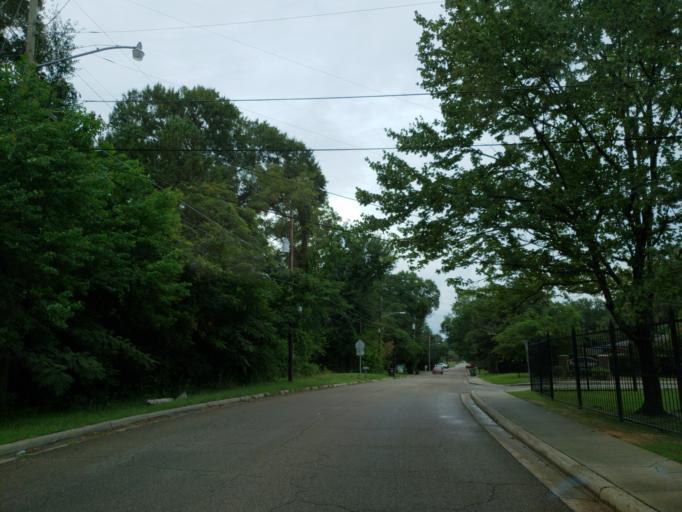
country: US
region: Mississippi
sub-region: Forrest County
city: Hattiesburg
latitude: 31.3139
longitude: -89.2994
